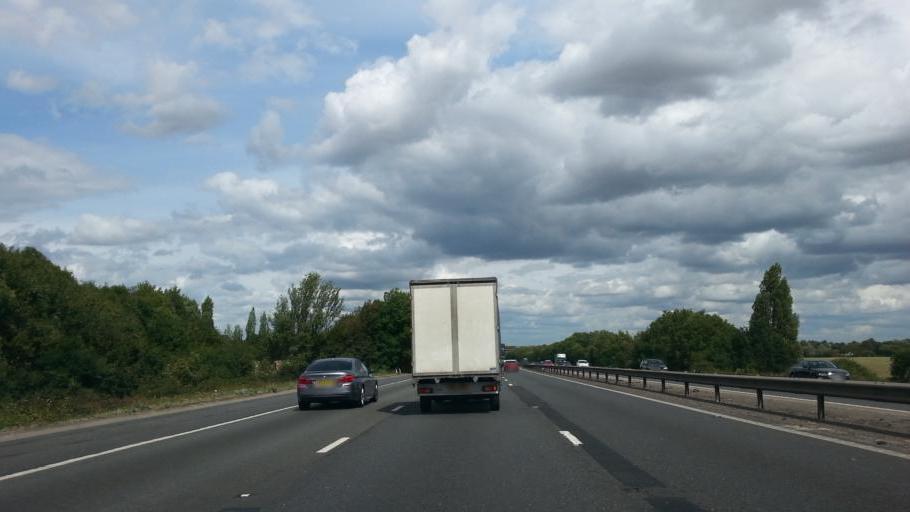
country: GB
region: England
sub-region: Essex
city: Harlow
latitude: 51.7663
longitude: 0.1536
